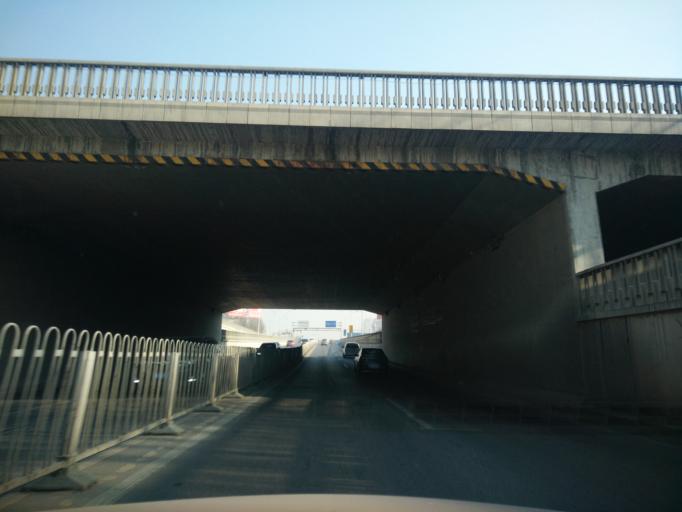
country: CN
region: Beijing
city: Jiugong
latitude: 39.8000
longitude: 116.5212
